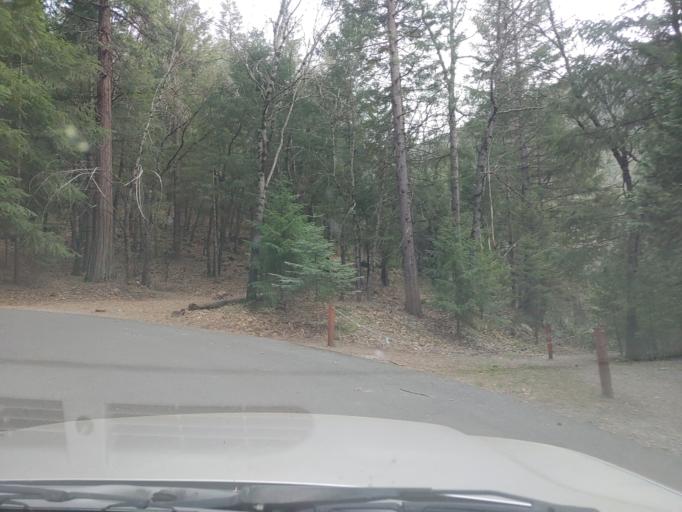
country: US
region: California
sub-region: Siskiyou County
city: Dunsmuir
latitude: 41.2252
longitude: -122.2793
